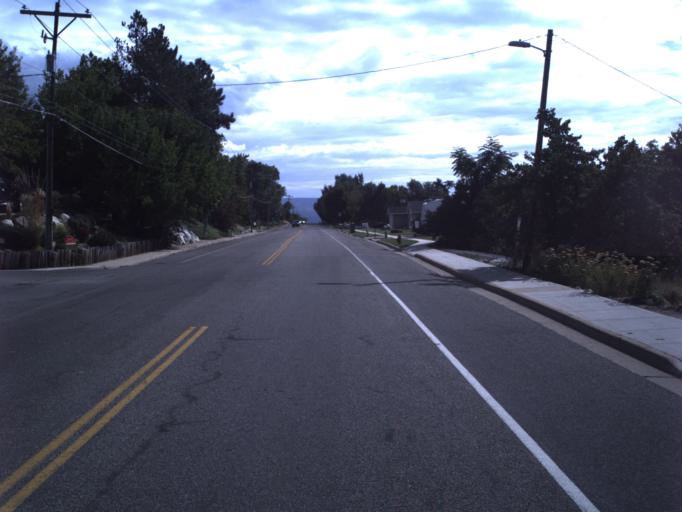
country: US
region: Utah
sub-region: Davis County
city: Farmington
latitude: 40.9670
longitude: -111.8834
